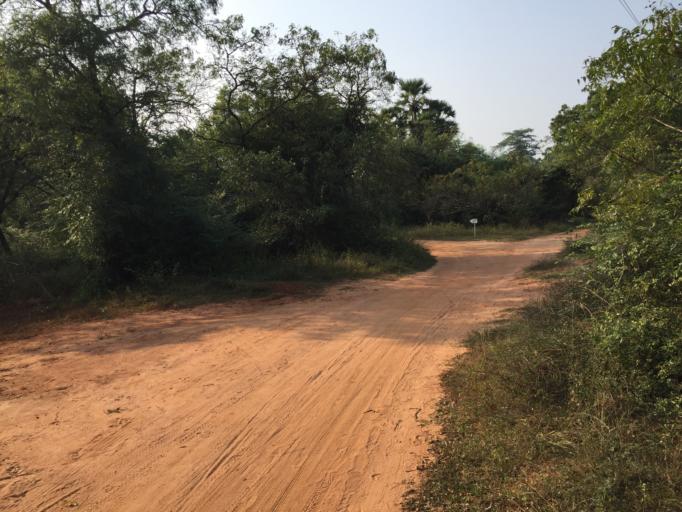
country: IN
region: Tamil Nadu
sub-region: Villupuram
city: Auroville
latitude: 12.0030
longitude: 79.8064
